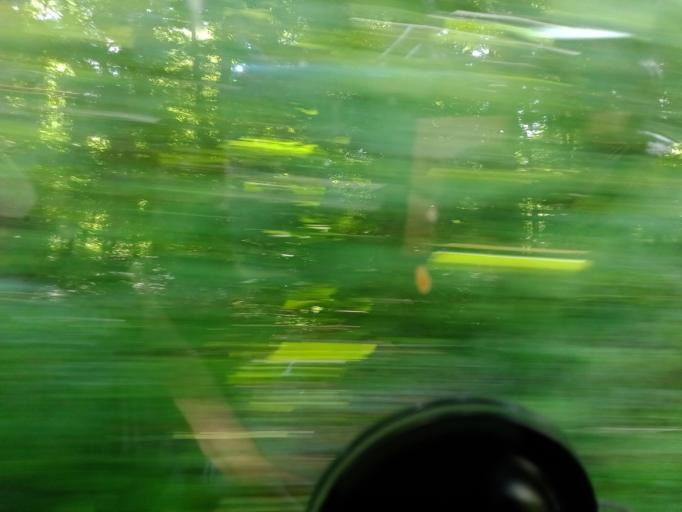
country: IE
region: Leinster
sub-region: Kilkenny
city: Thomastown
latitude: 52.5537
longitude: -7.0931
